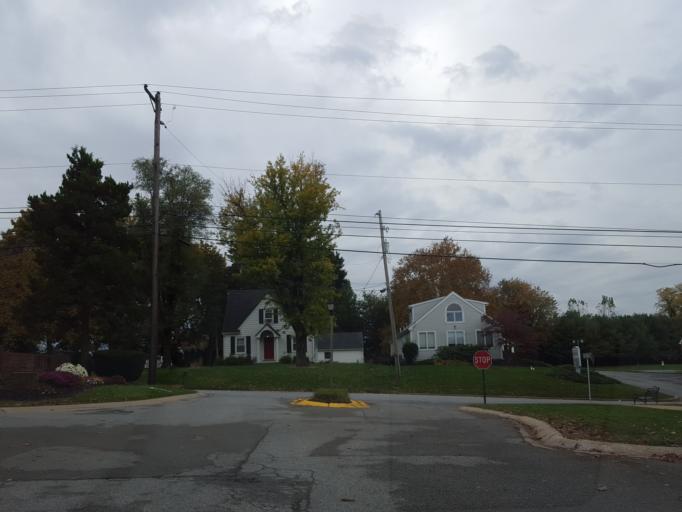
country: US
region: Pennsylvania
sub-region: York County
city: Valley View
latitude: 39.9383
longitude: -76.6897
